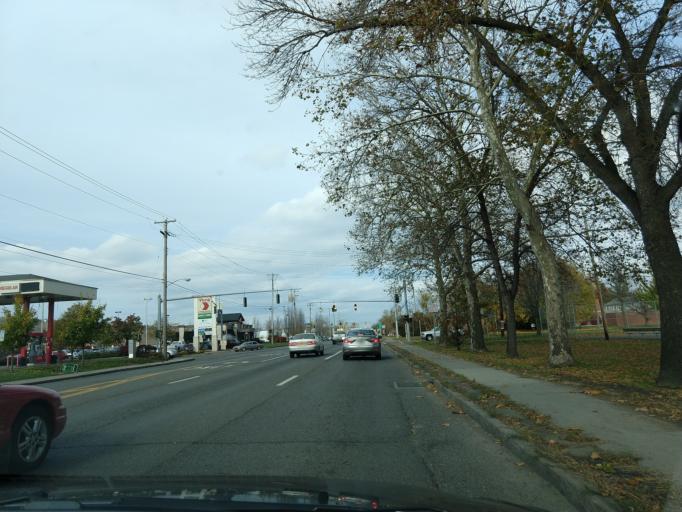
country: US
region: New York
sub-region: Tompkins County
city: South Hill
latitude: 42.4320
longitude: -76.5080
